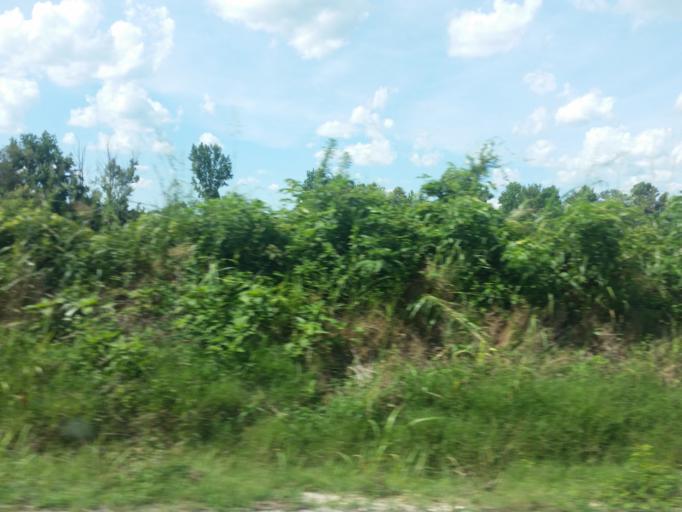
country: US
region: Tennessee
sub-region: Gibson County
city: Milan
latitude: 35.9731
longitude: -88.7105
